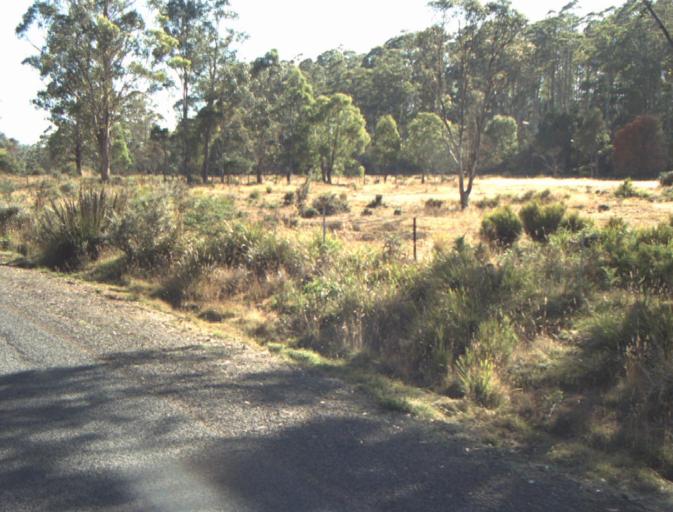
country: AU
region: Tasmania
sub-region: Launceston
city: Newstead
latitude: -41.3721
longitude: 147.2979
